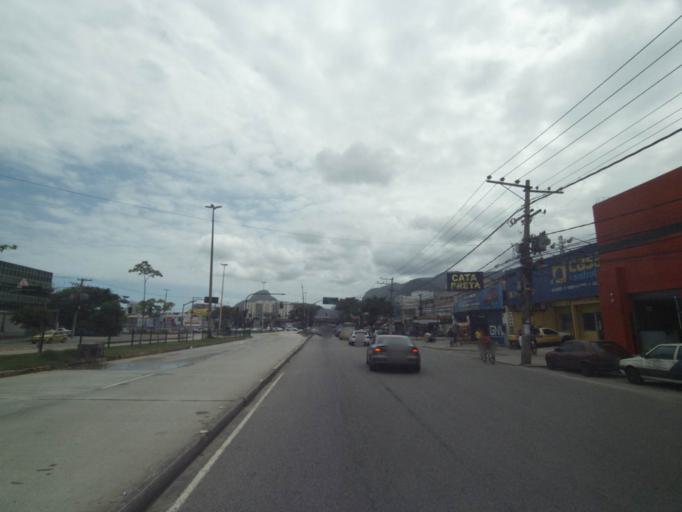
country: BR
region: Rio de Janeiro
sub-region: Nilopolis
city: Nilopolis
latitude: -22.9598
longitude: -43.3890
